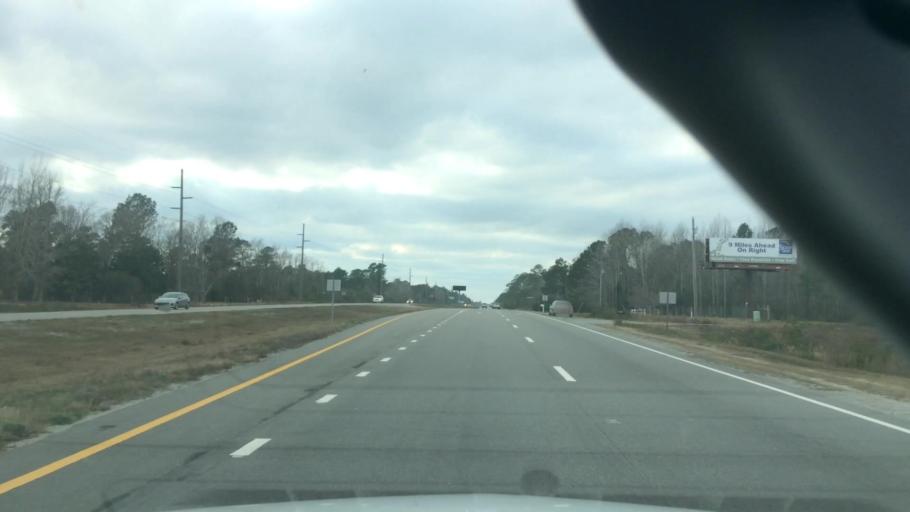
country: US
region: North Carolina
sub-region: Brunswick County
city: Sunset Beach
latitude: 33.9445
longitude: -78.5155
